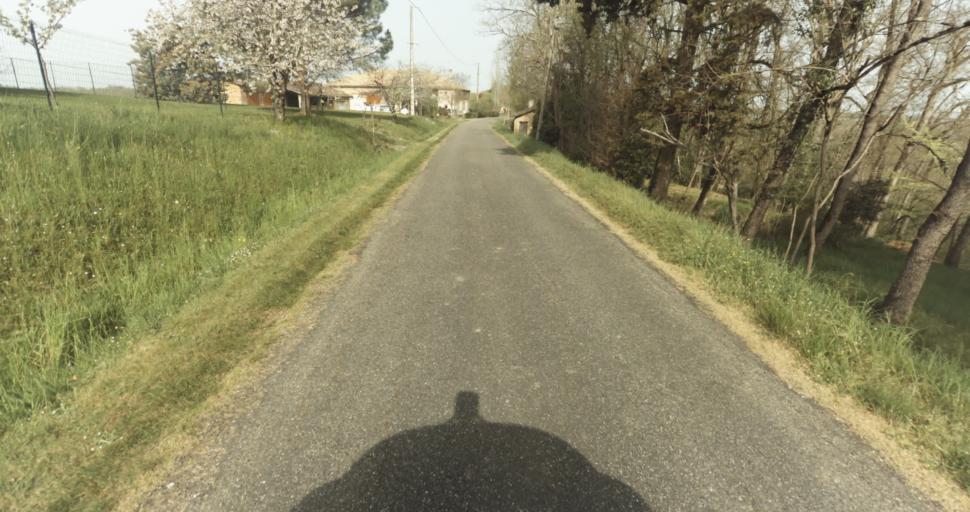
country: FR
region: Midi-Pyrenees
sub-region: Departement du Tarn-et-Garonne
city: Moissac
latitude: 44.1412
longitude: 1.0893
